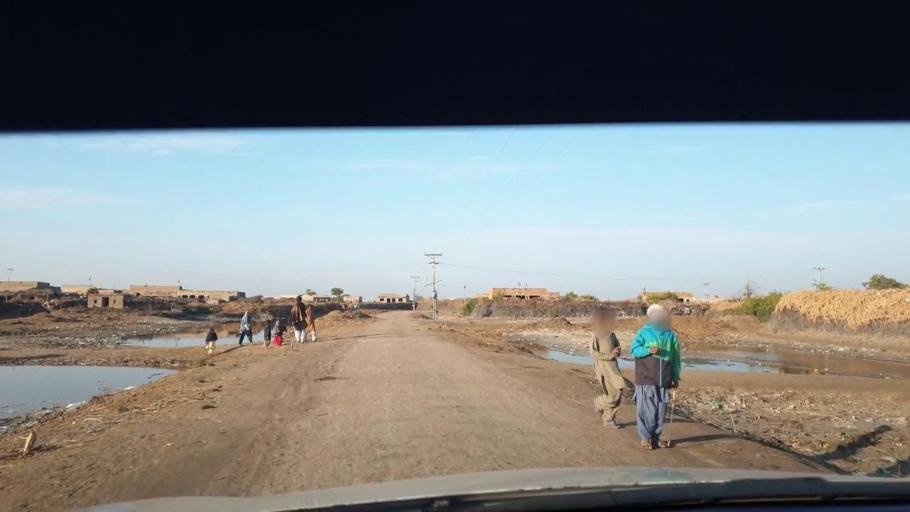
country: PK
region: Sindh
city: Berani
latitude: 25.8094
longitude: 68.9019
